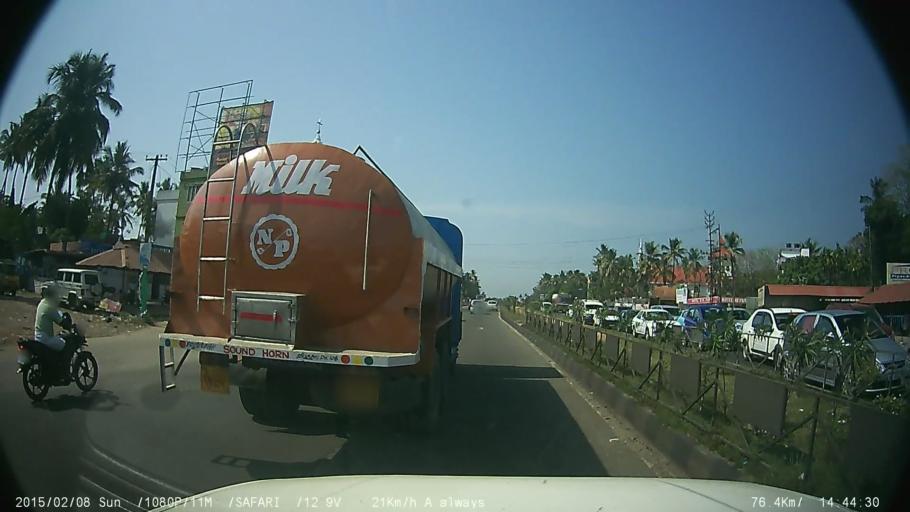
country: IN
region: Kerala
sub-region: Ernakulam
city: Angamali
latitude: 10.2106
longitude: 76.3816
